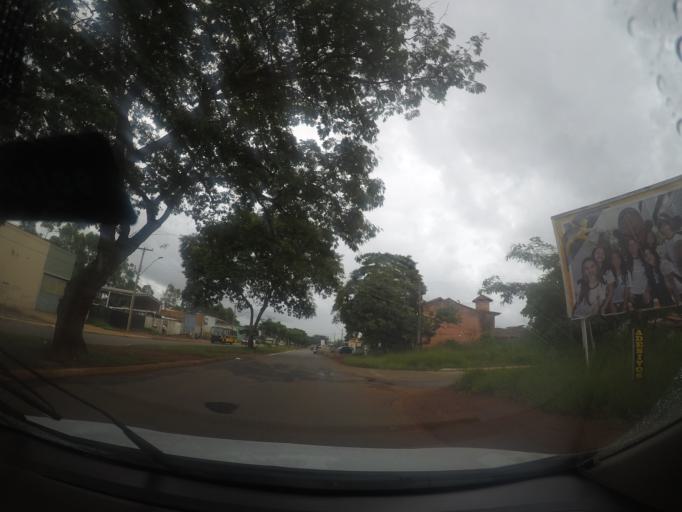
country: BR
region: Goias
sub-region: Trindade
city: Trindade
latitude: -16.6499
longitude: -49.3870
